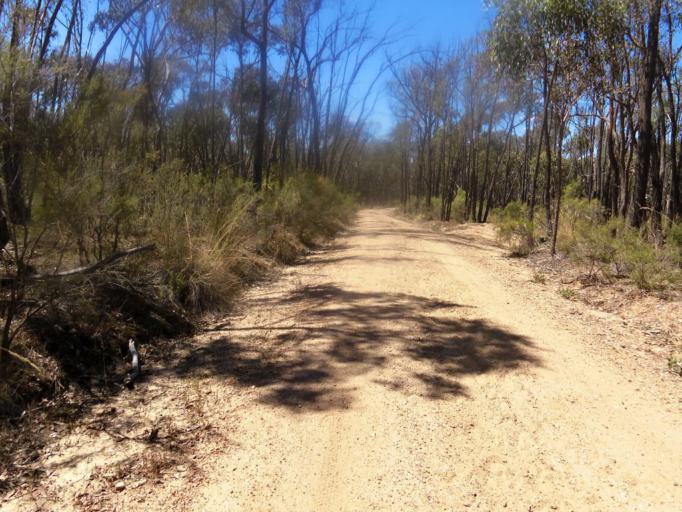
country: AU
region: Victoria
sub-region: Mount Alexander
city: Castlemaine
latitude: -37.0126
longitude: 144.1281
